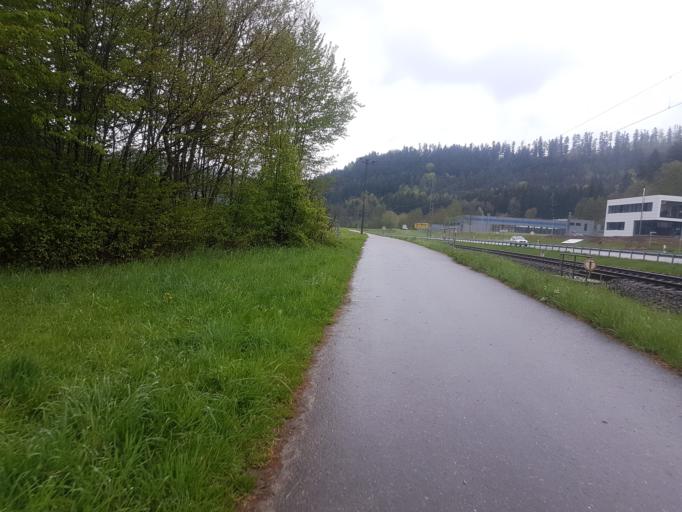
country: DE
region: Baden-Wuerttemberg
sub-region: Freiburg Region
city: Epfendorf
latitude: 48.2387
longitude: 8.6014
